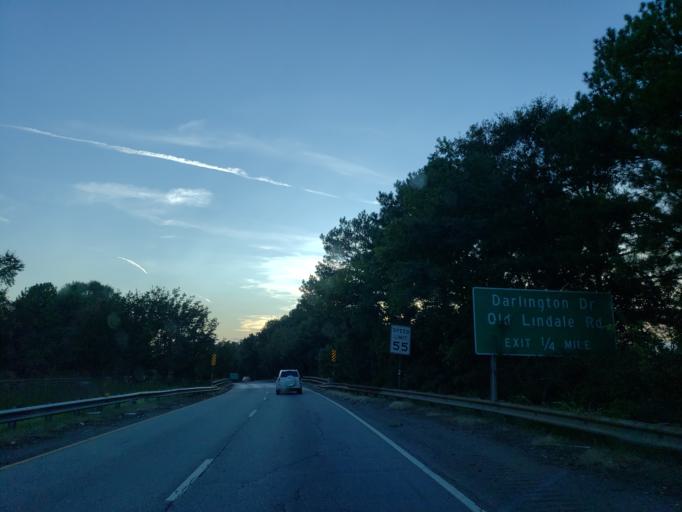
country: US
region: Georgia
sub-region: Floyd County
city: Rome
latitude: 34.2234
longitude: -85.1673
